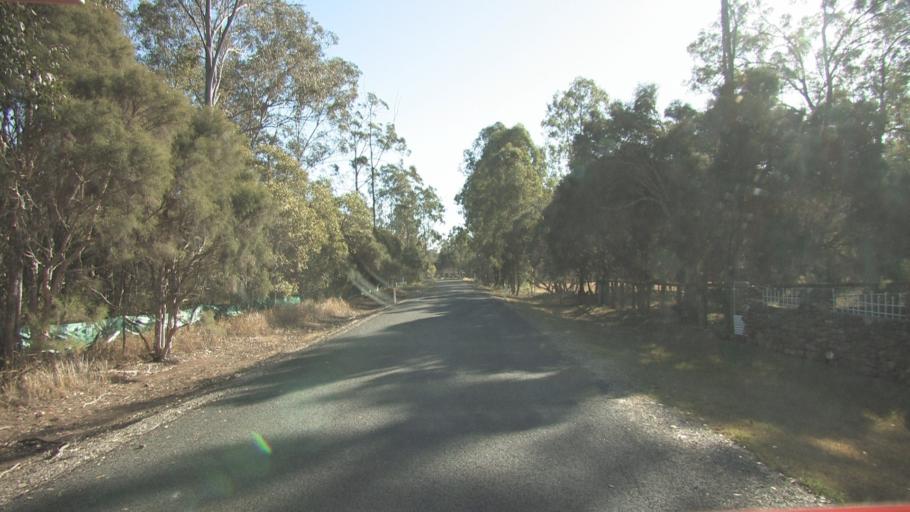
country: AU
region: Queensland
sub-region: Logan
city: Cedar Vale
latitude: -27.8414
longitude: 153.0026
